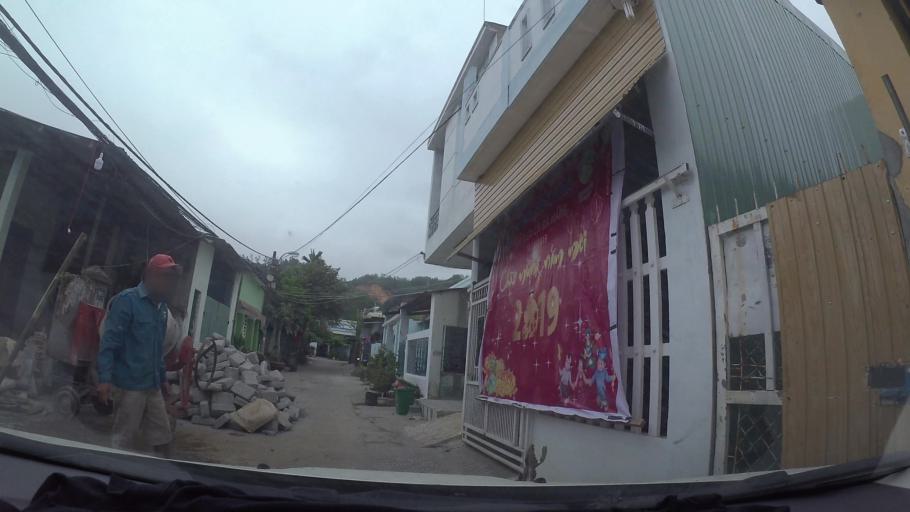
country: VN
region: Da Nang
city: Lien Chieu
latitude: 16.0681
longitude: 108.1428
